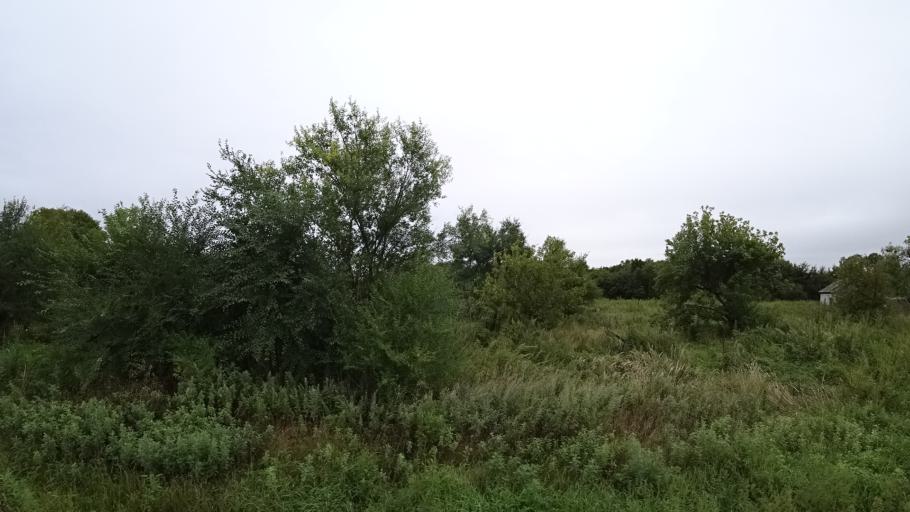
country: RU
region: Primorskiy
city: Monastyrishche
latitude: 44.0909
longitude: 132.5730
